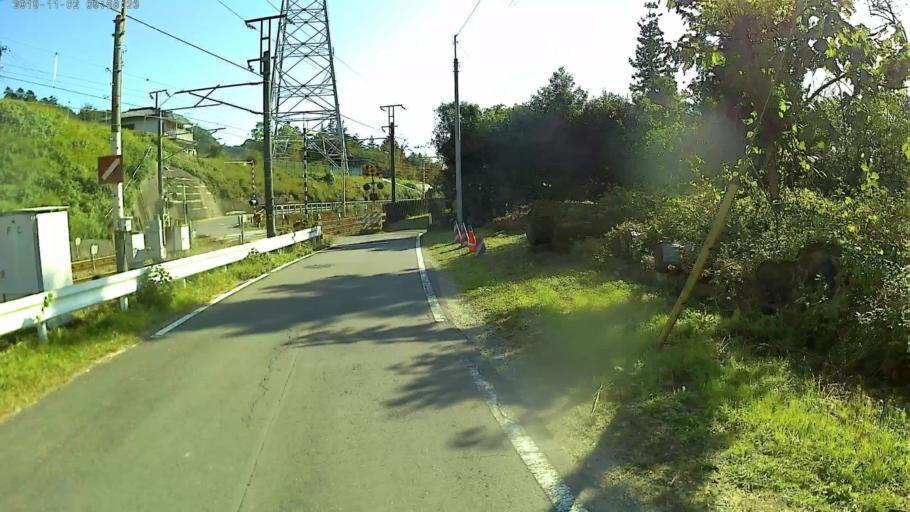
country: JP
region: Gunma
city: Annaka
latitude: 36.3201
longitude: 138.7796
